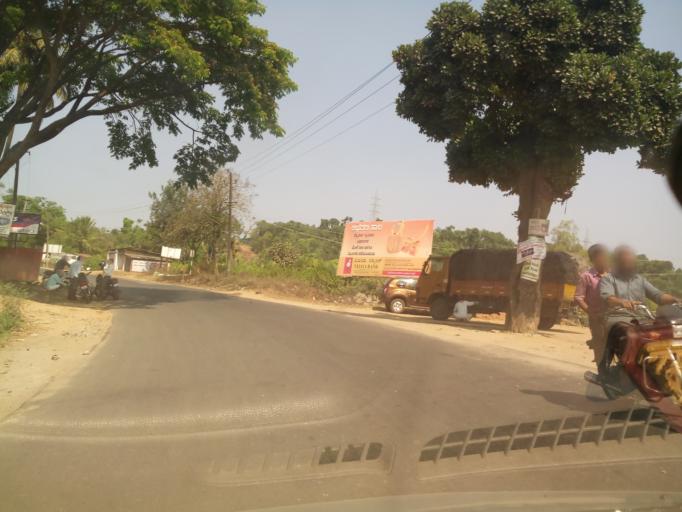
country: IN
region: Karnataka
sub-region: Hassan
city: Sakleshpur
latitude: 12.9448
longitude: 75.7989
